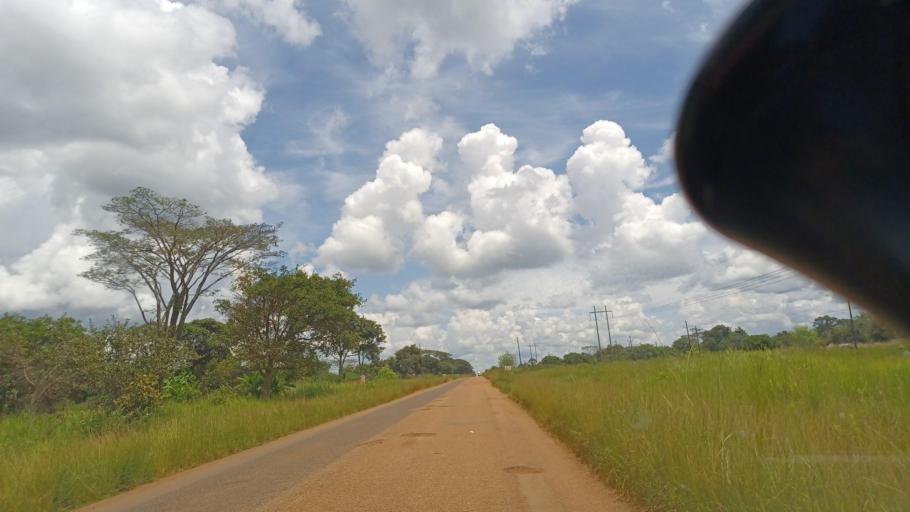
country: ZM
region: North-Western
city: Solwezi
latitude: -12.4864
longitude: 26.1937
